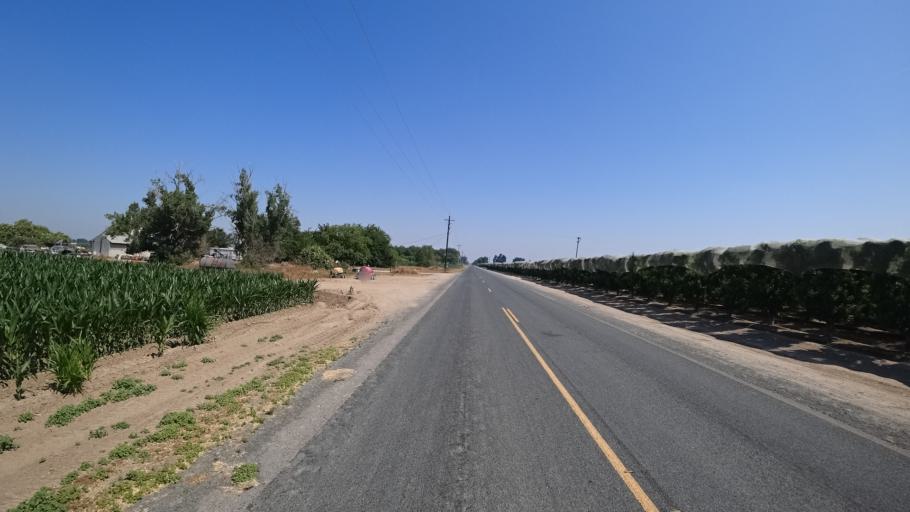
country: US
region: California
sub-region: Fresno County
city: Kingsburg
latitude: 36.4463
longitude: -119.5286
